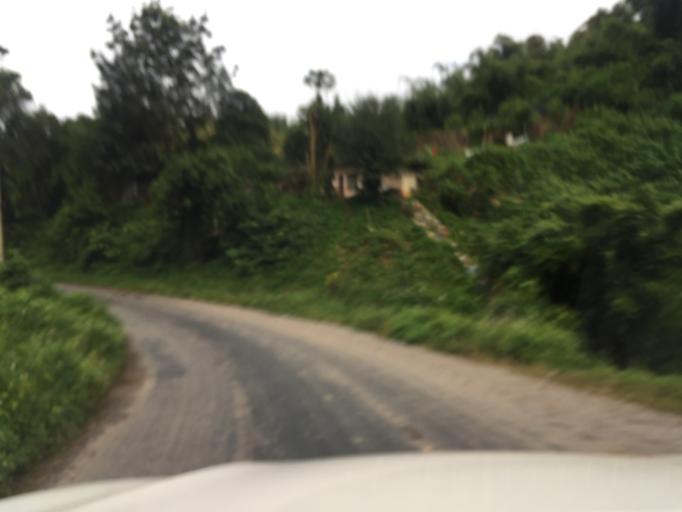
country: LA
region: Phongsali
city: Khoa
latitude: 21.1042
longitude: 102.2741
